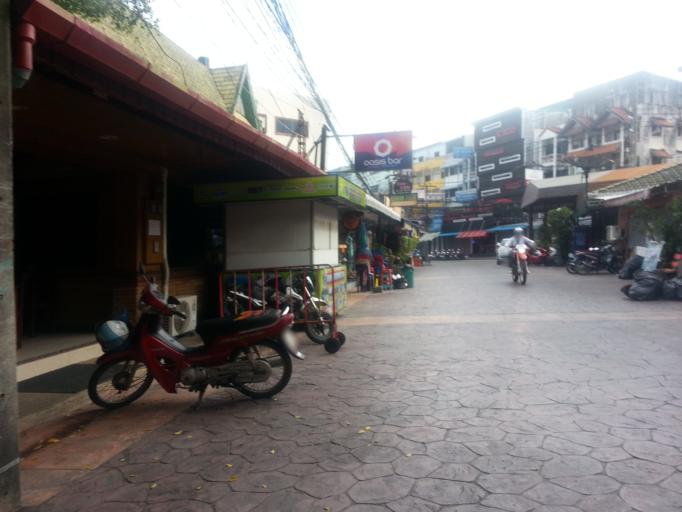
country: TH
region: Phuket
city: Patong
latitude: 7.8893
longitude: 98.2951
